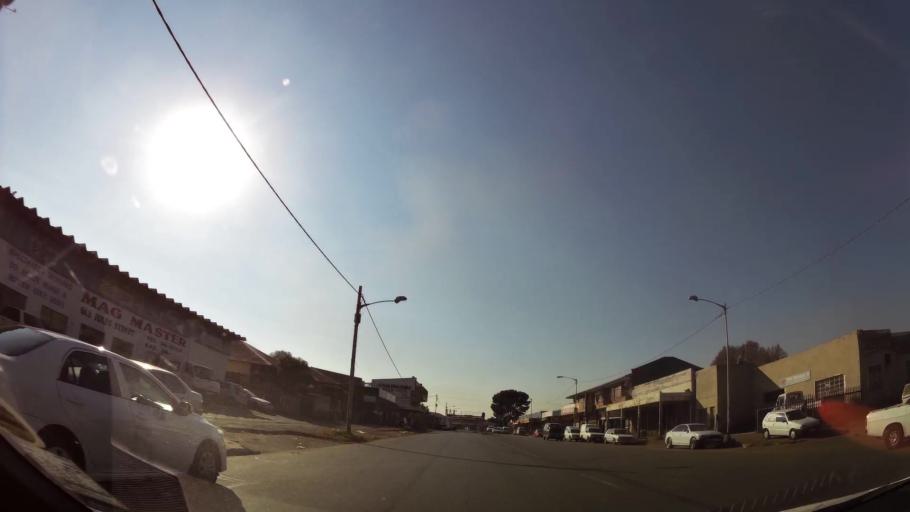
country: ZA
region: Gauteng
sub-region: Ekurhuleni Metropolitan Municipality
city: Germiston
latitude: -26.2010
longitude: 28.1182
